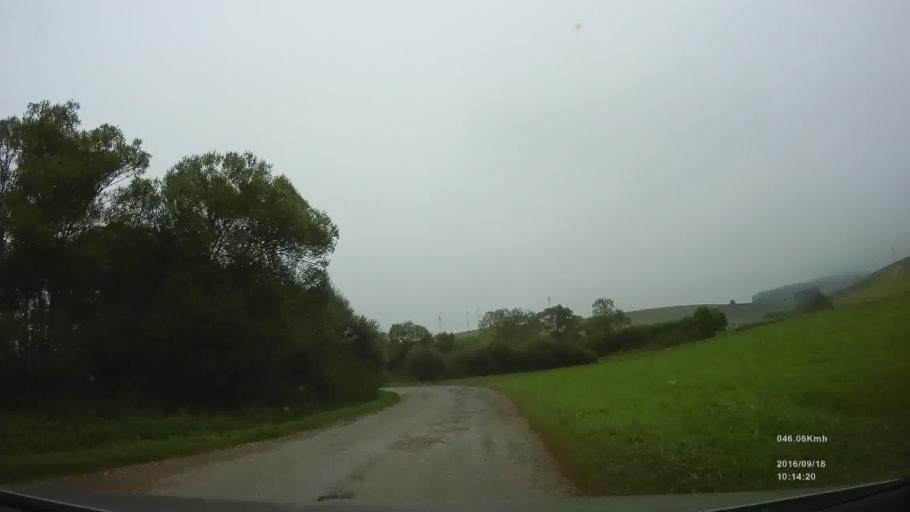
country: SK
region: Kosicky
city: Spisska Nova Ves
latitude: 48.9401
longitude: 20.6268
